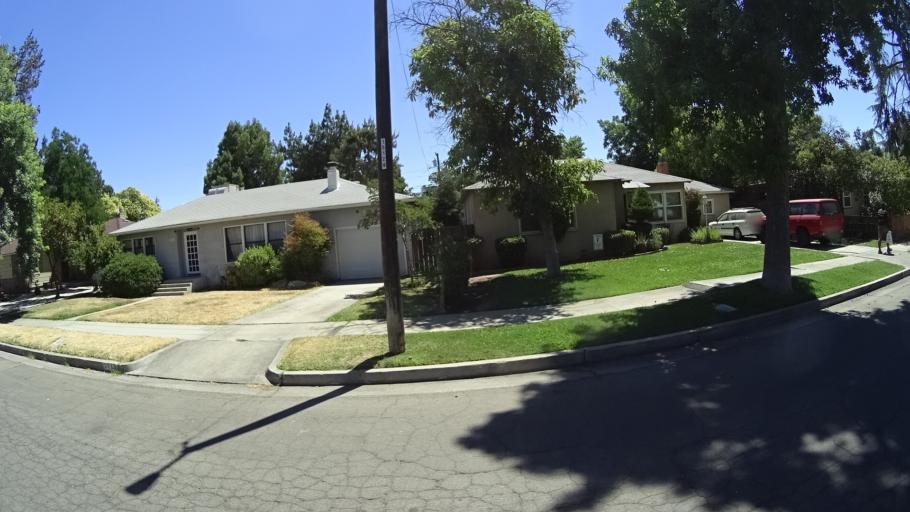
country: US
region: California
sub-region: Fresno County
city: Fresno
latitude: 36.7762
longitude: -119.8131
